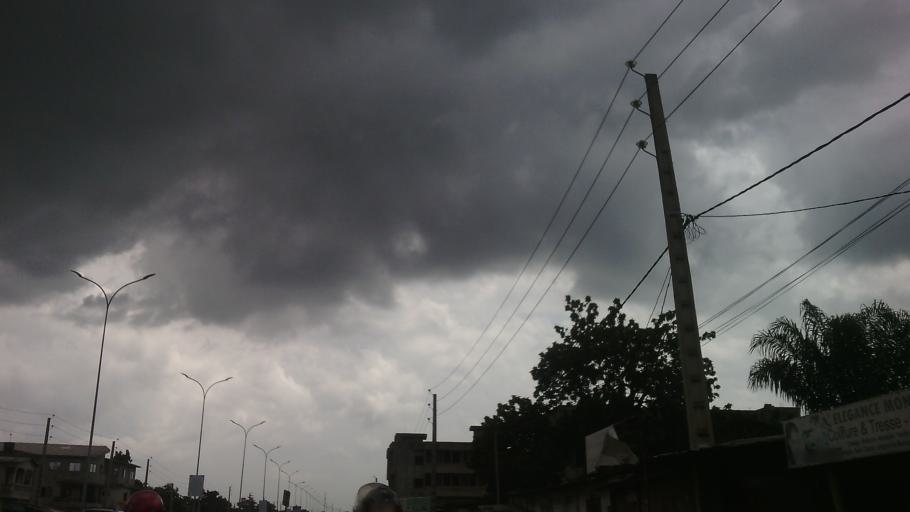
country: BJ
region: Atlantique
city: Abomey-Calavi
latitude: 6.4677
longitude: 2.3562
